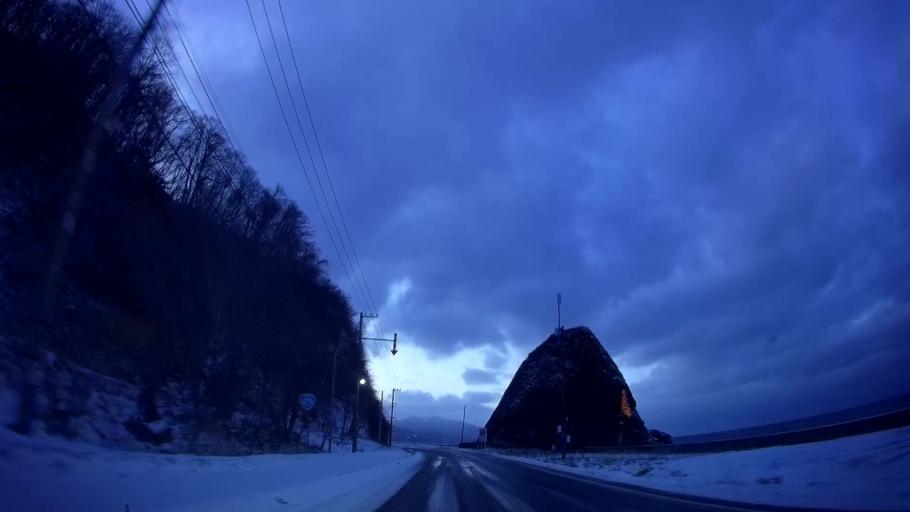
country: JP
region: Hokkaido
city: Hakodate
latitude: 41.8929
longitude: 141.0468
